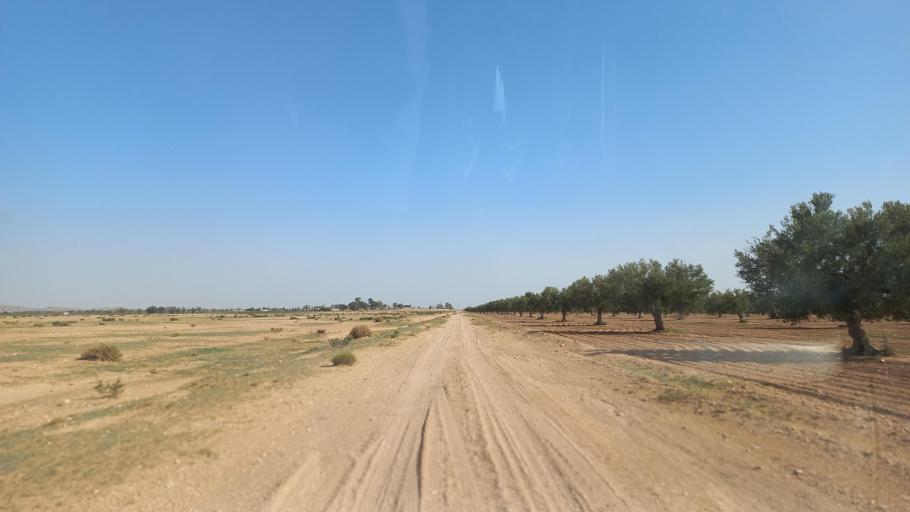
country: TN
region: Al Qasrayn
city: Kasserine
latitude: 35.3039
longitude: 9.0245
